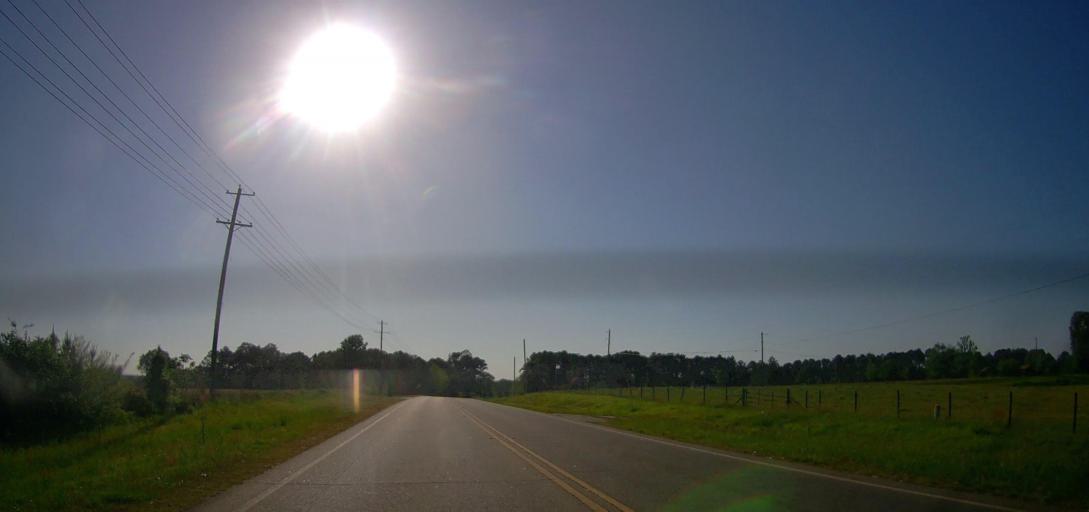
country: US
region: Georgia
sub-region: Ben Hill County
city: Fitzgerald
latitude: 31.6931
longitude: -83.2862
